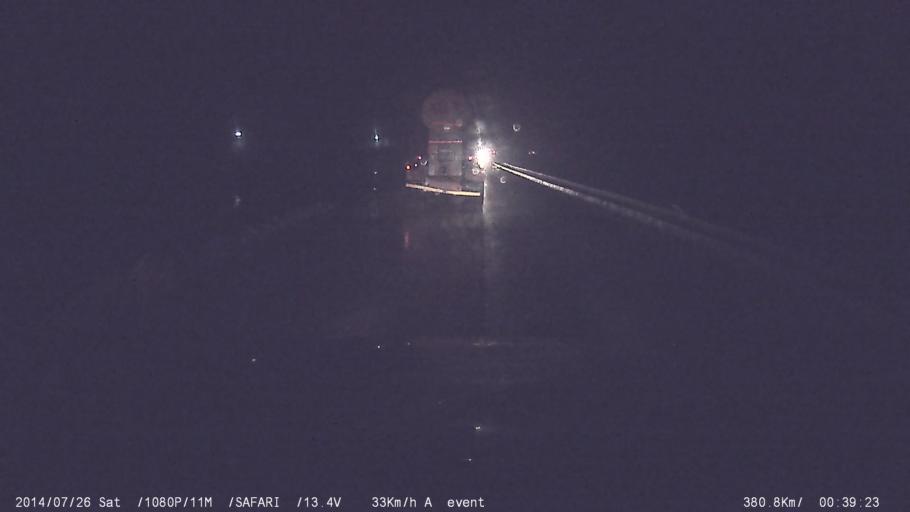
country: IN
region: Kerala
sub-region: Palakkad district
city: Chittur
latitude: 10.8204
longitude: 76.8108
